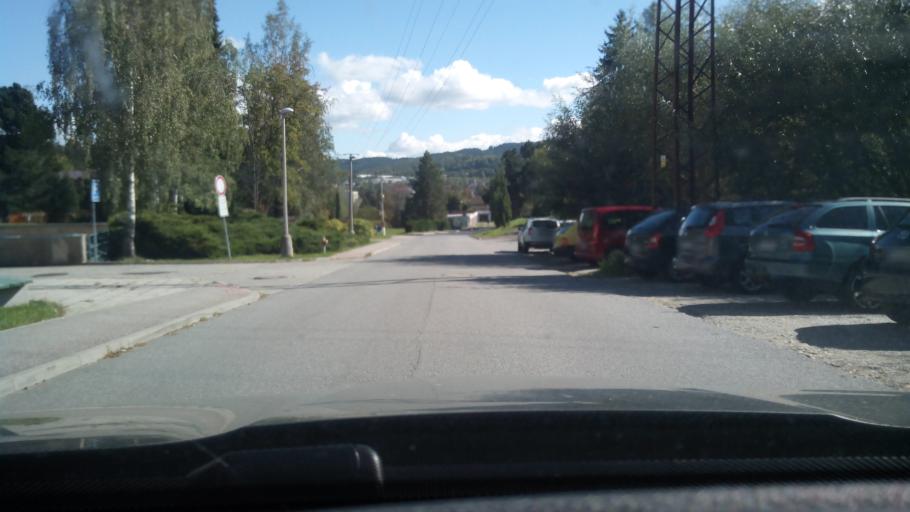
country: CZ
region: Jihocesky
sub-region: Okres Prachatice
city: Vimperk
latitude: 49.0589
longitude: 13.7752
